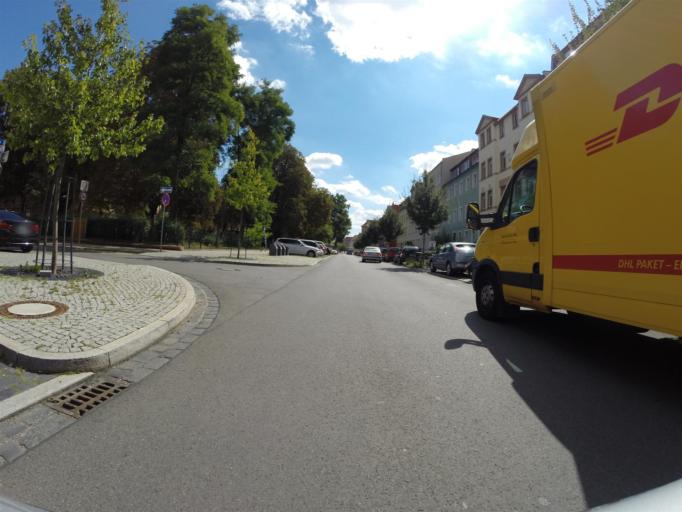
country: DE
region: Thuringia
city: Erfurt
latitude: 50.9853
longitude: 11.0213
